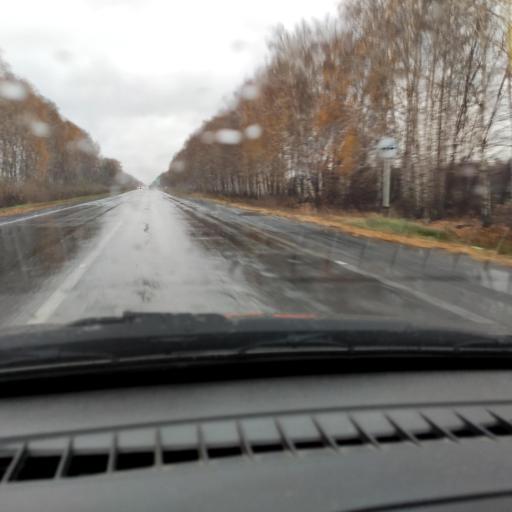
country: RU
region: Samara
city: Tol'yatti
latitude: 53.5930
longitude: 49.3277
